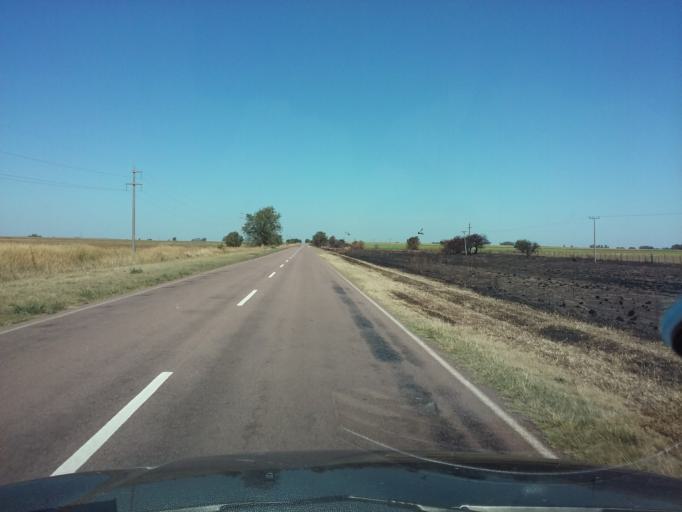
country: AR
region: La Pampa
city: Uriburu
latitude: -36.3860
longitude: -63.9431
